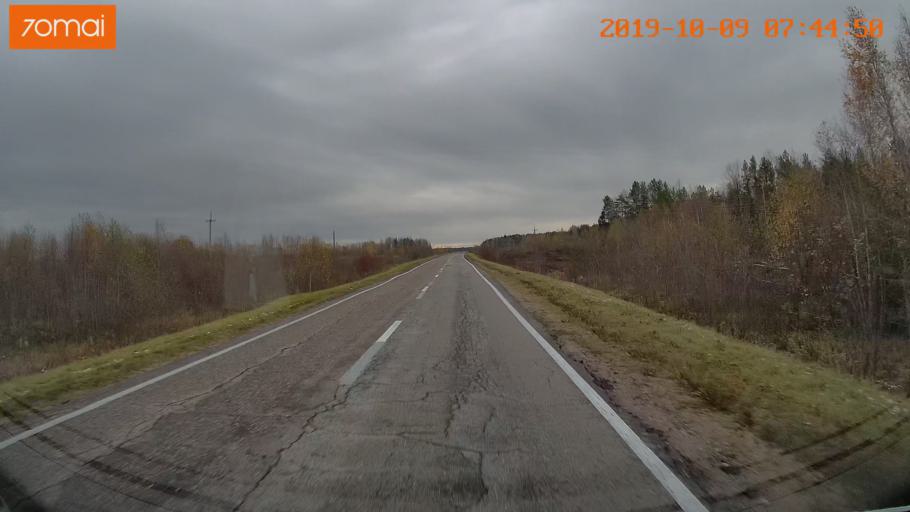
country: RU
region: Jaroslavl
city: Kukoboy
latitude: 58.6511
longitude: 39.7542
